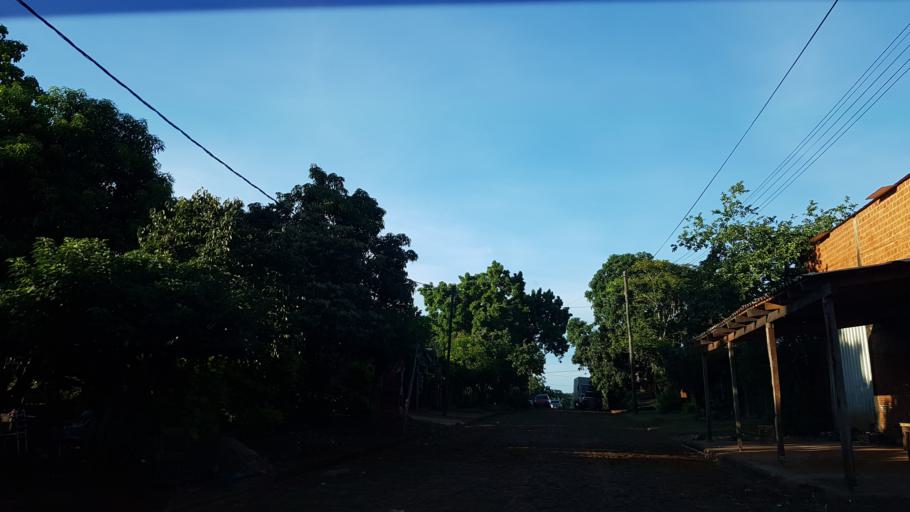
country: AR
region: Misiones
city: Puerto Libertad
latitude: -25.9240
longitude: -54.5825
